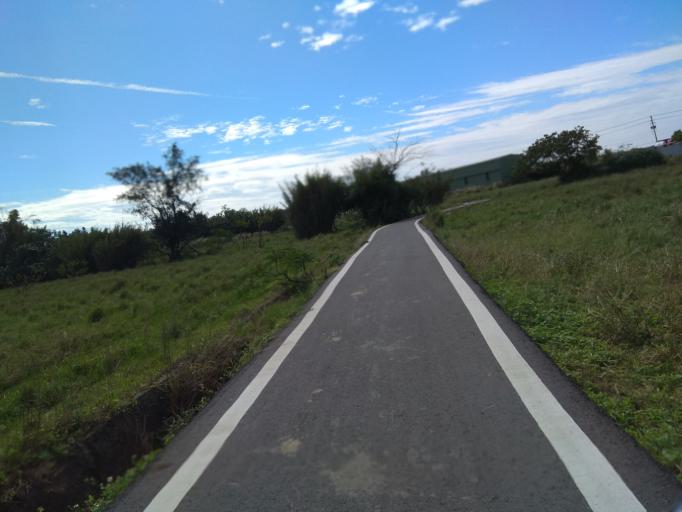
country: TW
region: Taiwan
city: Taoyuan City
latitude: 25.0479
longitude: 121.1210
